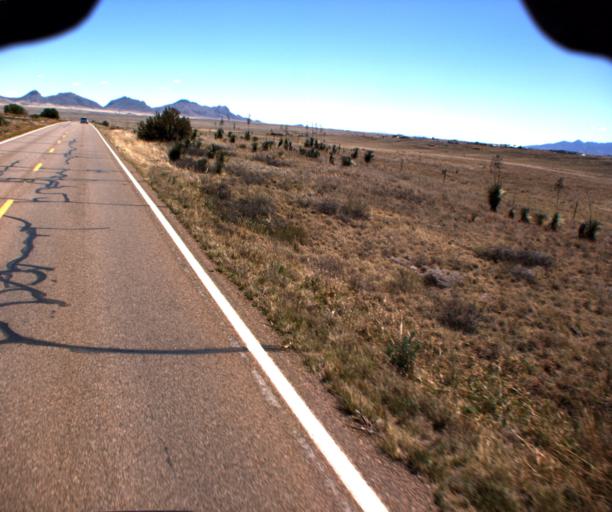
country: US
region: Arizona
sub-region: Cochise County
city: Huachuca City
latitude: 31.6812
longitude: -110.6407
